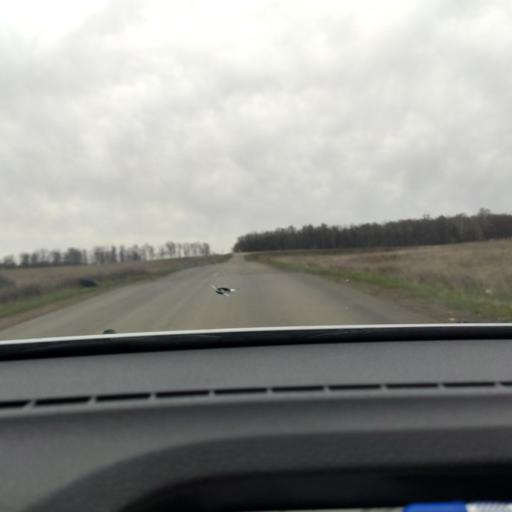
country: RU
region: Bashkortostan
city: Avdon
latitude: 54.6357
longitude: 55.6037
